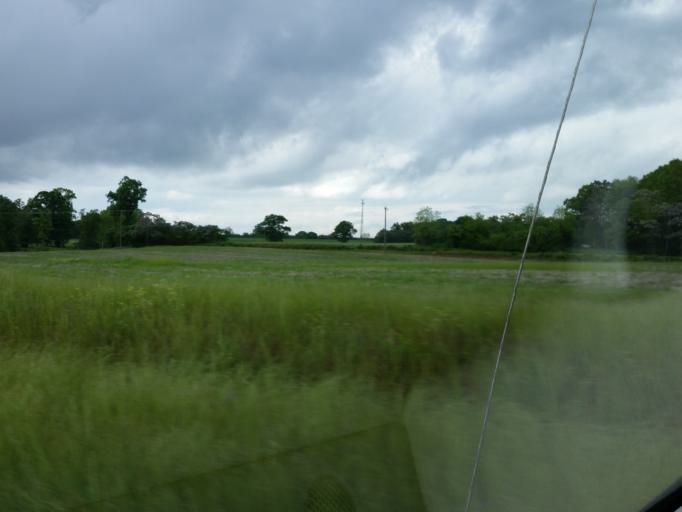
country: US
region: Georgia
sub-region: Dooly County
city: Unadilla
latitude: 32.3397
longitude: -83.7783
